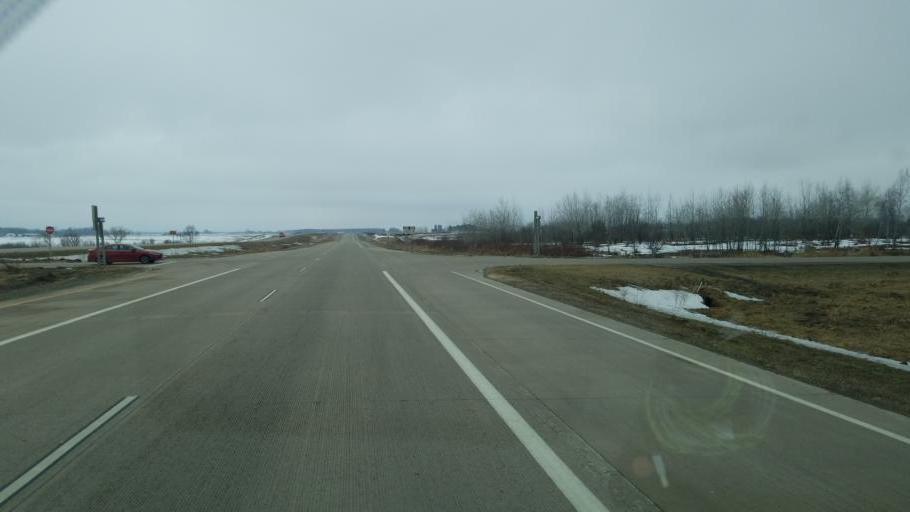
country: US
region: Wisconsin
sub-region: Wood County
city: Marshfield
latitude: 44.6202
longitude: -90.0044
